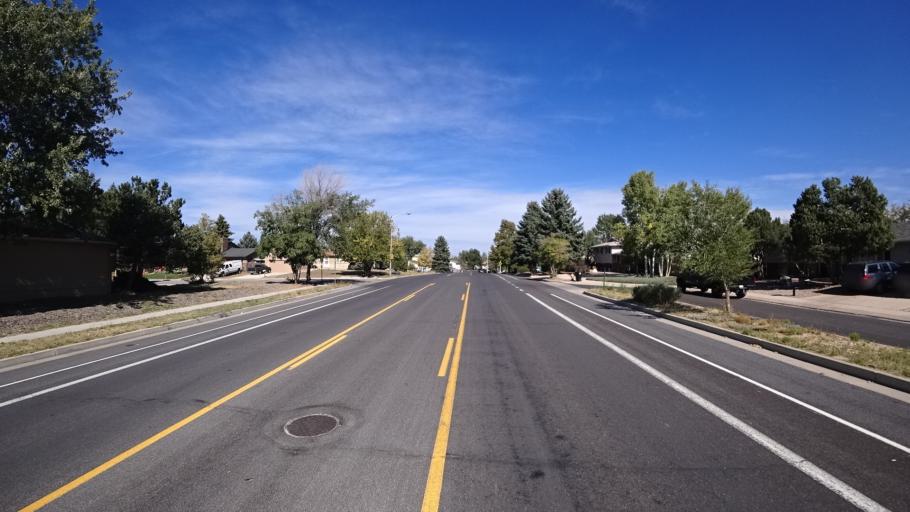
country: US
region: Colorado
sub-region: El Paso County
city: Cimarron Hills
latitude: 38.9194
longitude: -104.7660
